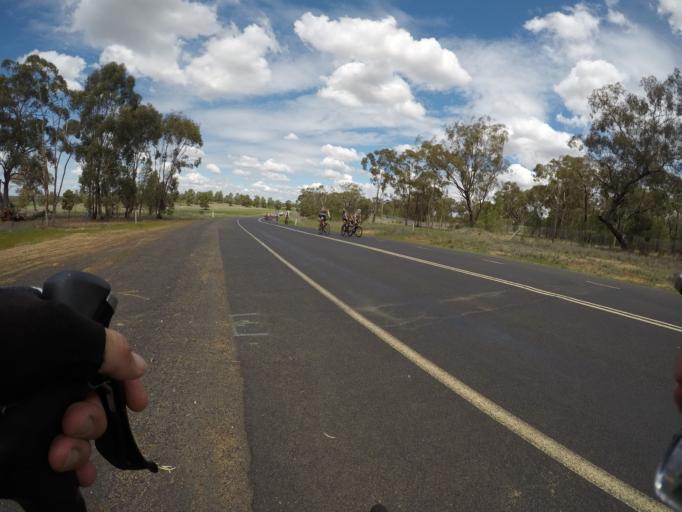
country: AU
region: New South Wales
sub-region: Dubbo Municipality
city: Dubbo
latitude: -32.2856
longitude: 148.5972
